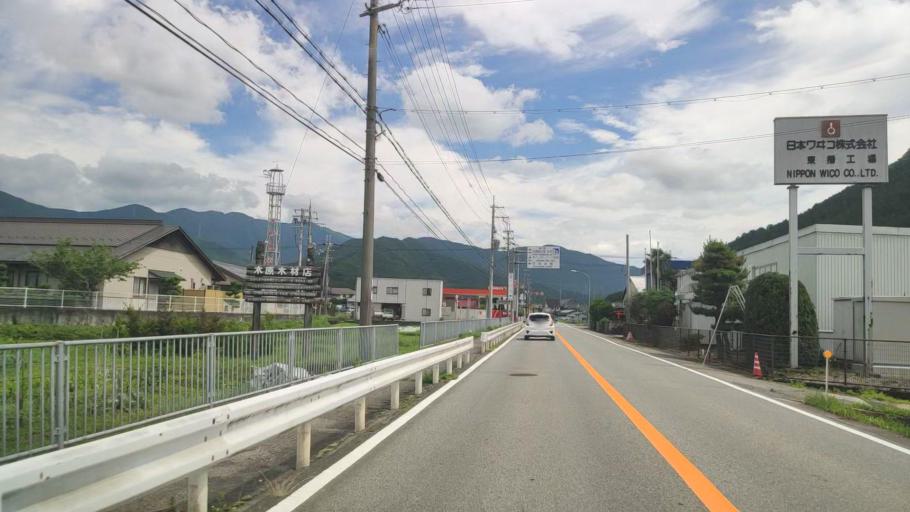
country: JP
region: Hyogo
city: Nishiwaki
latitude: 35.0820
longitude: 134.8909
